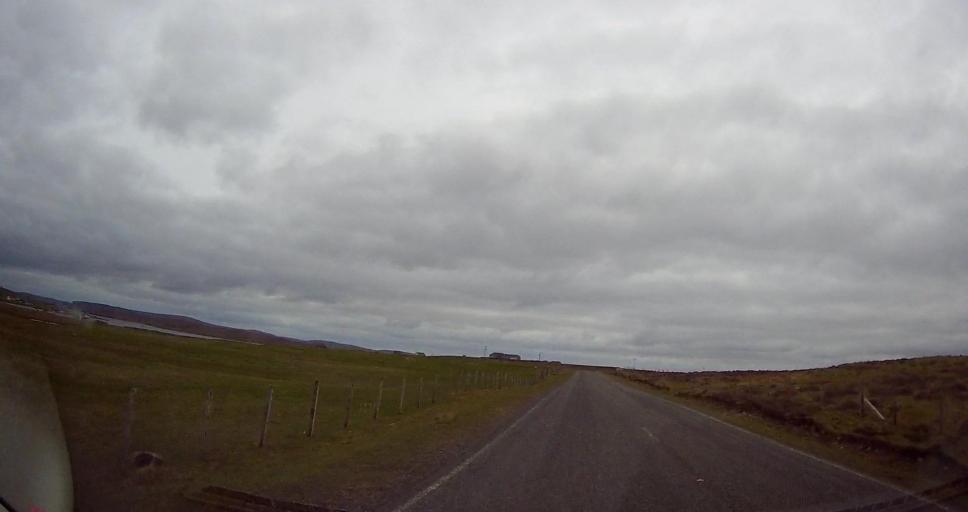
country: GB
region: Scotland
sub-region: Shetland Islands
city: Shetland
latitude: 60.6990
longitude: -0.9212
